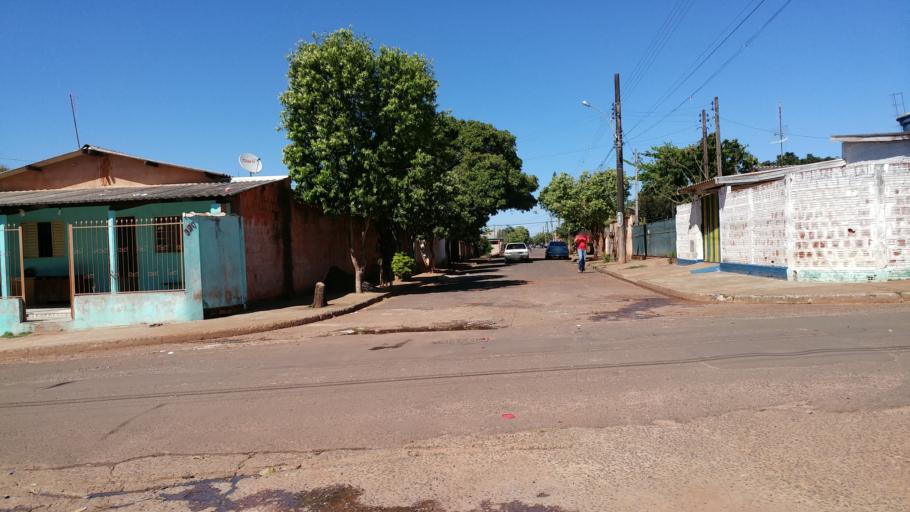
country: BR
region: Sao Paulo
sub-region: Paraguacu Paulista
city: Paraguacu Paulista
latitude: -22.4085
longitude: -50.5657
